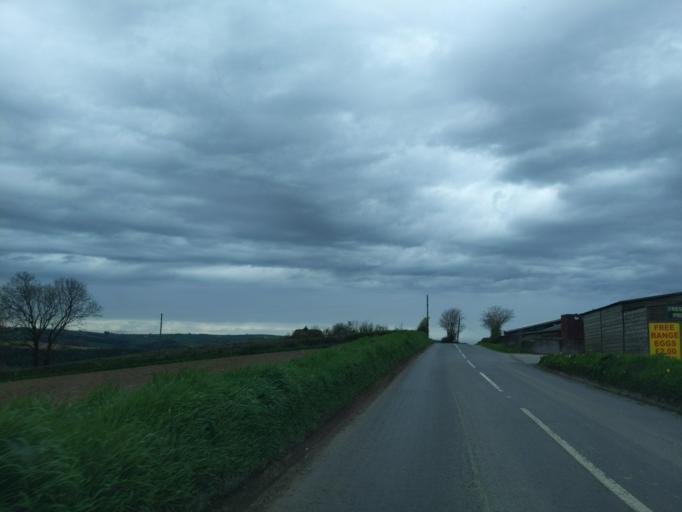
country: GB
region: England
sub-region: Devon
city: Great Torrington
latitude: 50.9298
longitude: -4.0780
